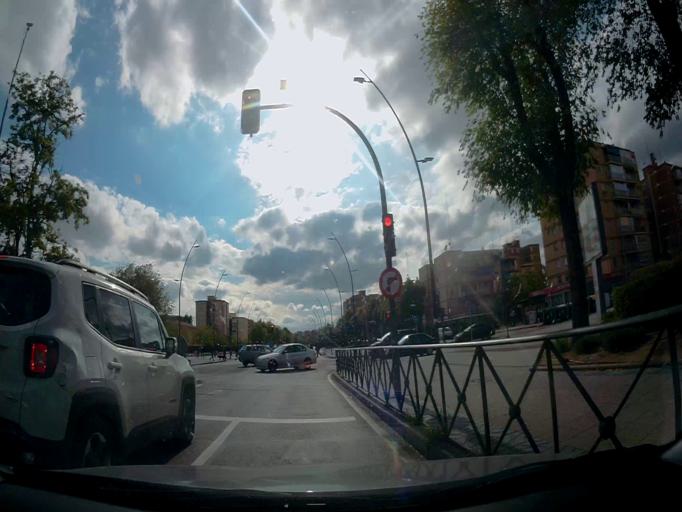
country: ES
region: Madrid
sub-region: Provincia de Madrid
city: Mostoles
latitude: 40.3272
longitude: -3.8626
